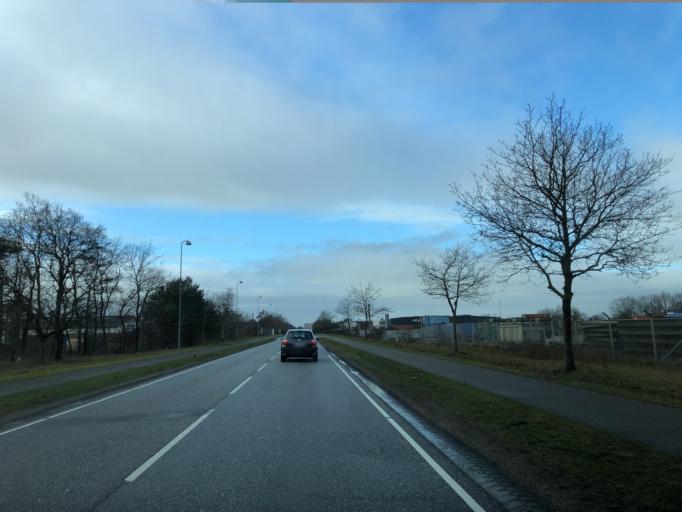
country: DK
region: Central Jutland
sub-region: Skive Kommune
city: Skive
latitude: 56.5427
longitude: 9.0267
